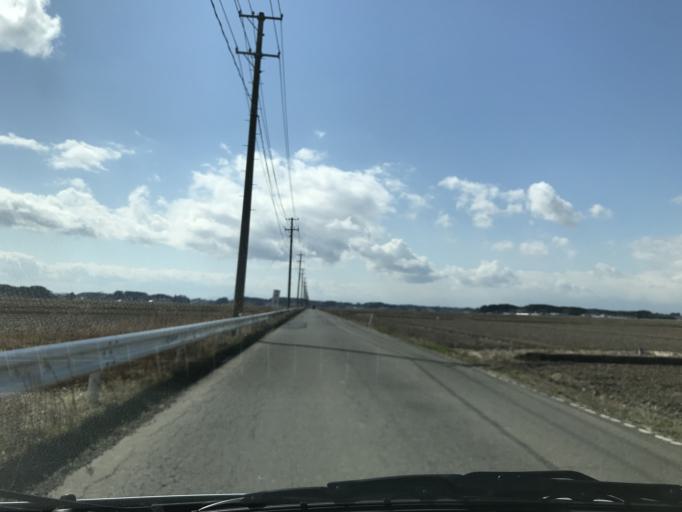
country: JP
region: Miyagi
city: Wakuya
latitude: 38.6858
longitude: 141.1704
